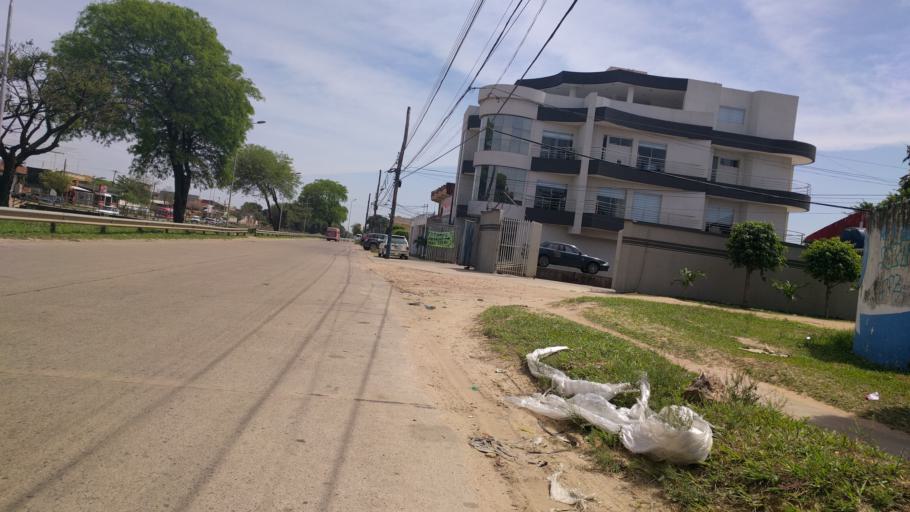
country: BO
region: Santa Cruz
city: Santa Cruz de la Sierra
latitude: -17.8185
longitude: -63.2243
